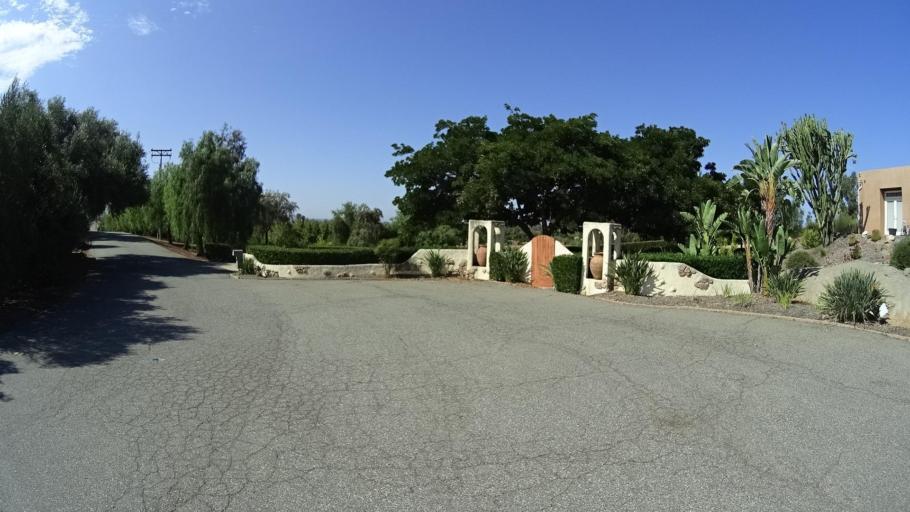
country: US
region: California
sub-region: San Diego County
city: Valley Center
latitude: 33.2911
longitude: -117.0191
